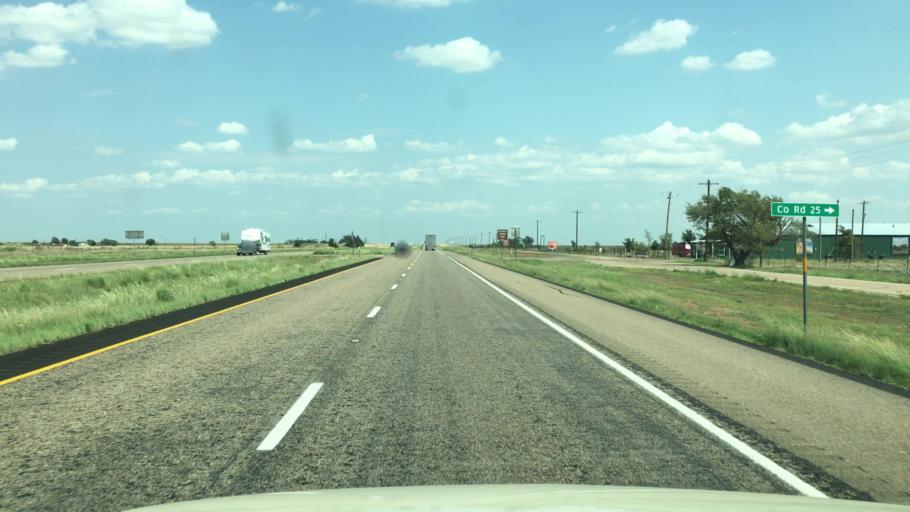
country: US
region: Texas
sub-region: Armstrong County
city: Claude
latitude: 35.0339
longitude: -101.1839
